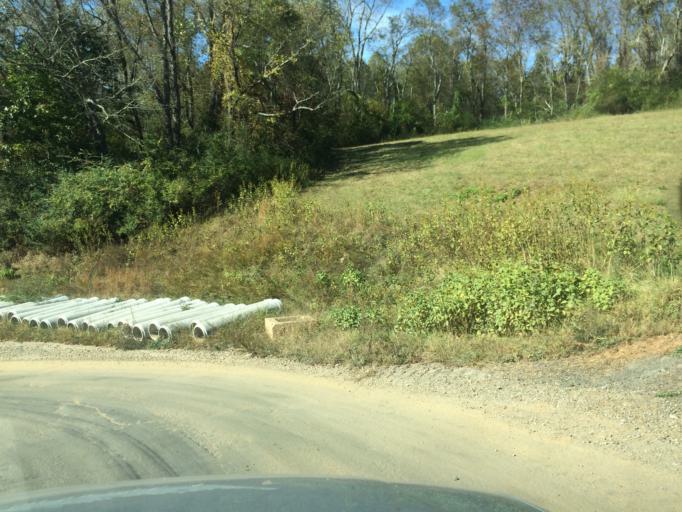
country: US
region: North Carolina
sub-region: Buncombe County
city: Woodfin
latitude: 35.6431
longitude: -82.5928
